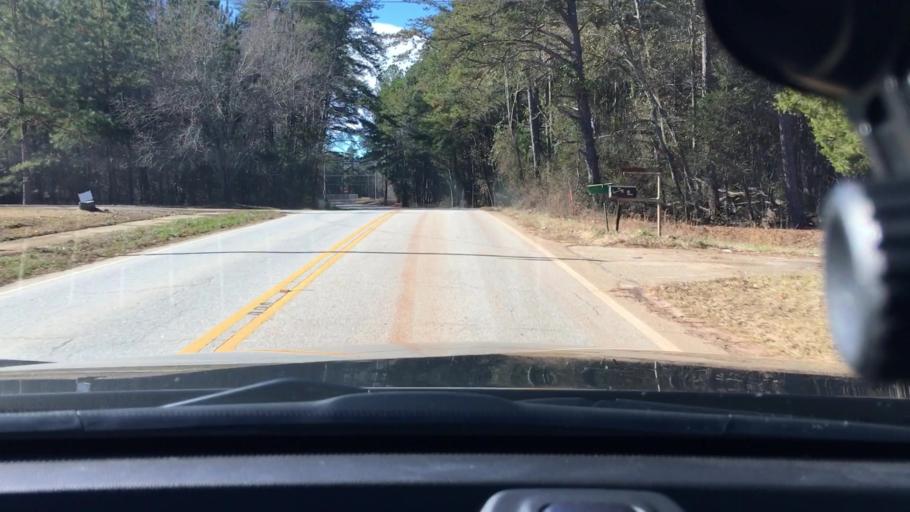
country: US
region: South Carolina
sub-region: Spartanburg County
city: Pacolet
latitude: 34.9146
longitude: -81.7657
